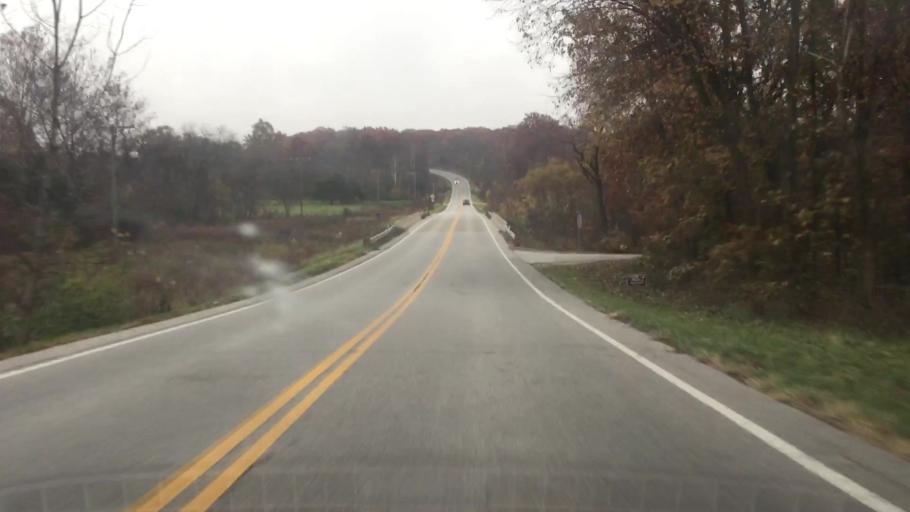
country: US
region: Missouri
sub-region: Callaway County
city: Fulton
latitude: 38.8824
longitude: -92.0920
